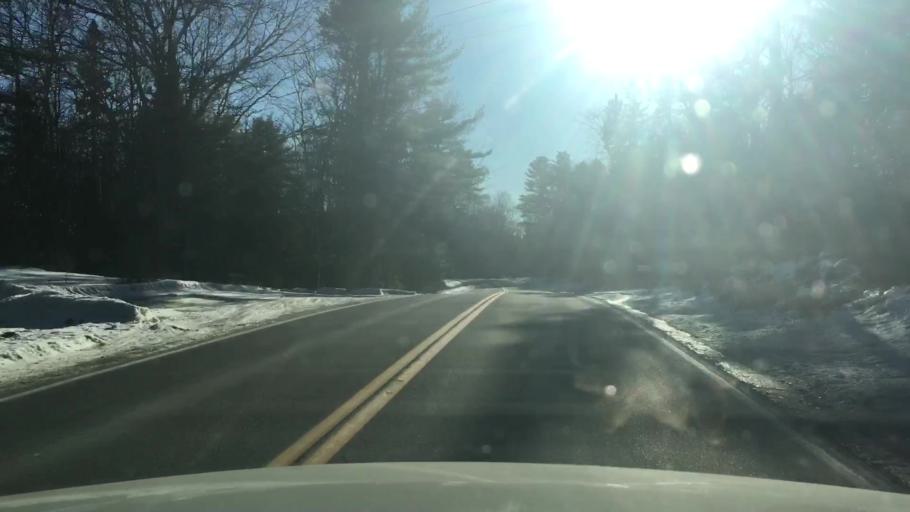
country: US
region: Maine
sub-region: Hancock County
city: Orland
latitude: 44.5150
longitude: -68.7521
